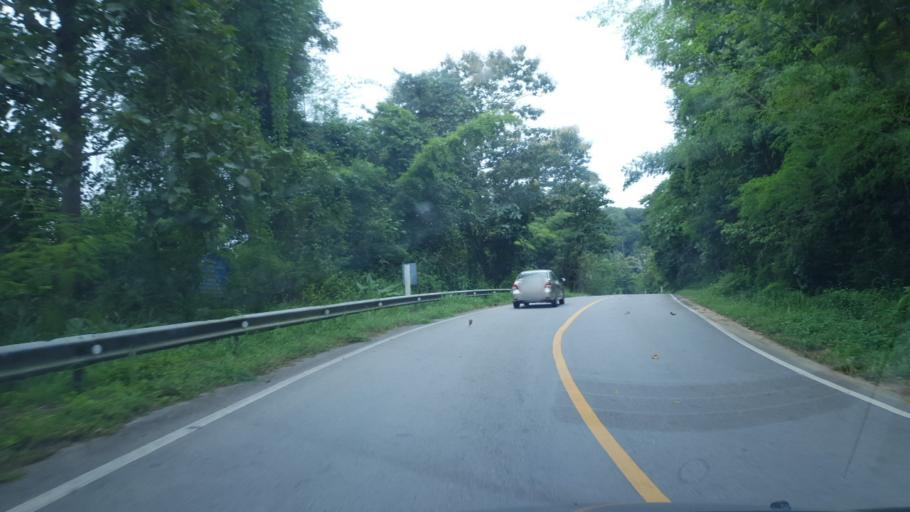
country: TH
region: Mae Hong Son
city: Khun Yuam
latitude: 18.7117
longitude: 97.9117
